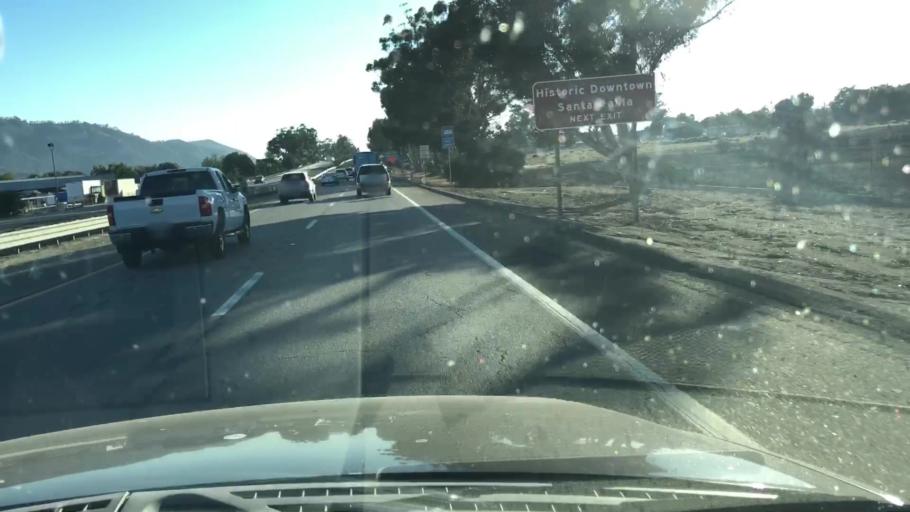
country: US
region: California
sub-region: Ventura County
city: Santa Paula
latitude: 34.3584
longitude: -119.0438
